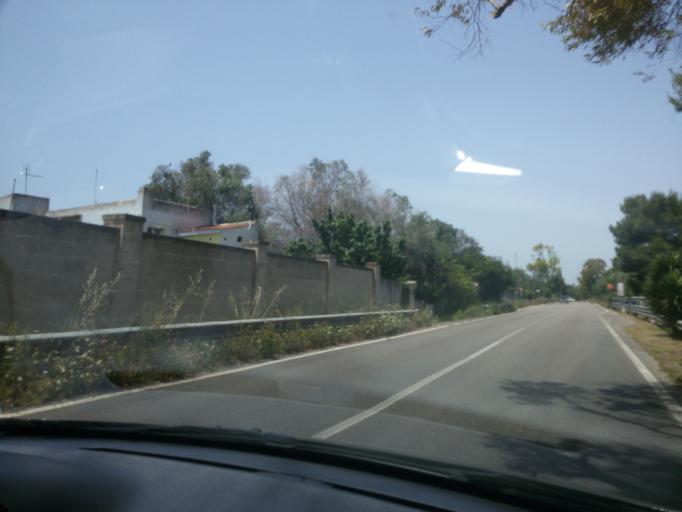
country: IT
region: Apulia
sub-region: Provincia di Lecce
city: Porto Cesareo
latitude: 40.2571
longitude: 17.9262
